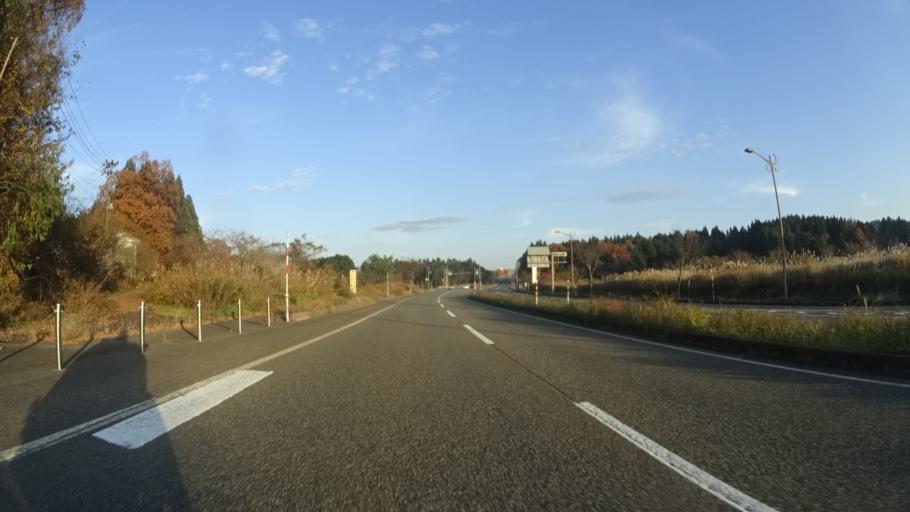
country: JP
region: Niigata
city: Nagaoka
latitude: 37.4510
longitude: 138.7605
